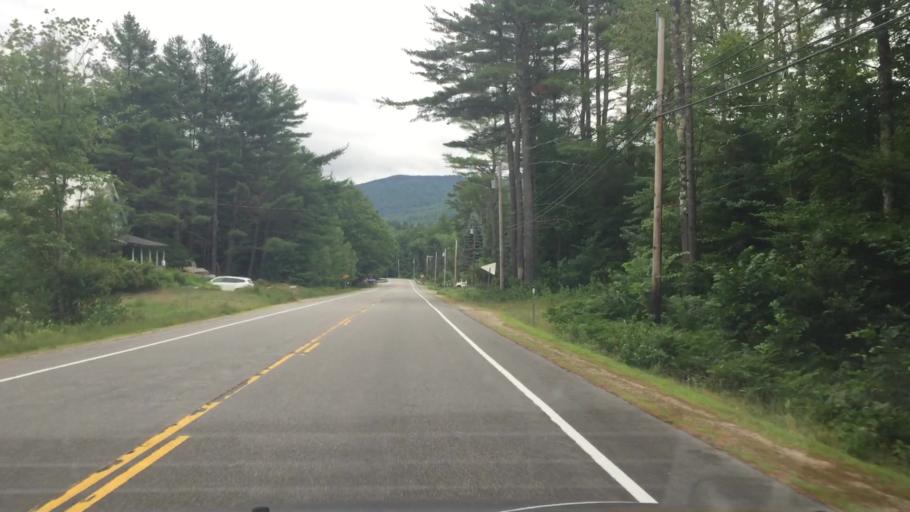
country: US
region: New Hampshire
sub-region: Carroll County
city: Tamworth
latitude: 43.8260
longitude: -71.3164
